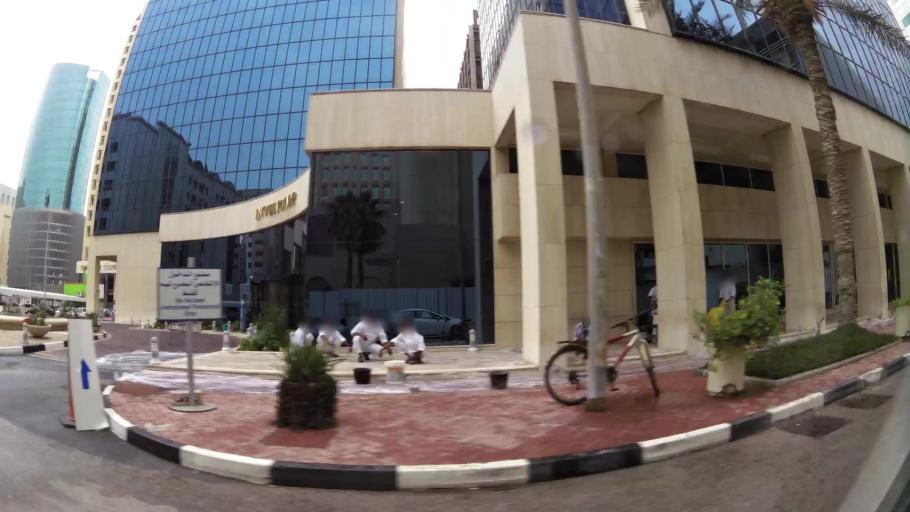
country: BH
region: Manama
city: Manama
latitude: 26.2414
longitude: 50.5894
